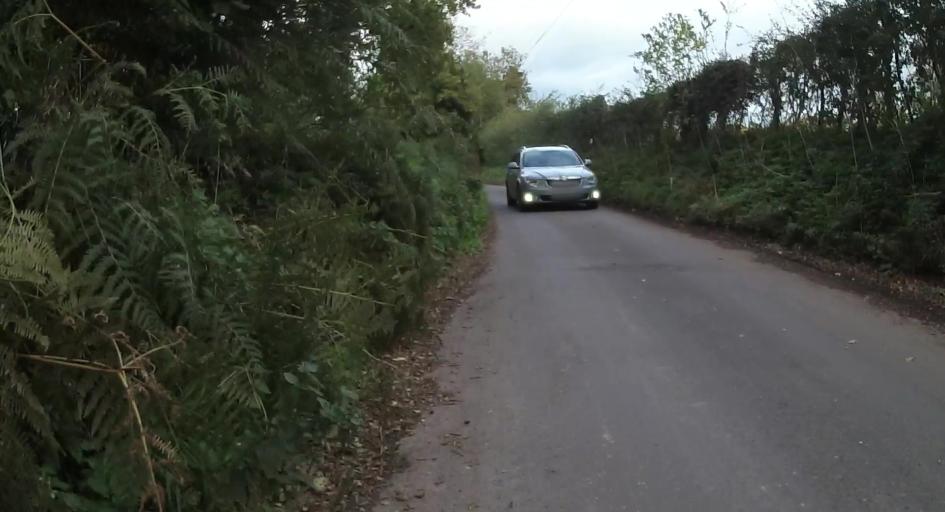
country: GB
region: England
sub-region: Hampshire
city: Kingsley
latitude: 51.1484
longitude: -0.9192
